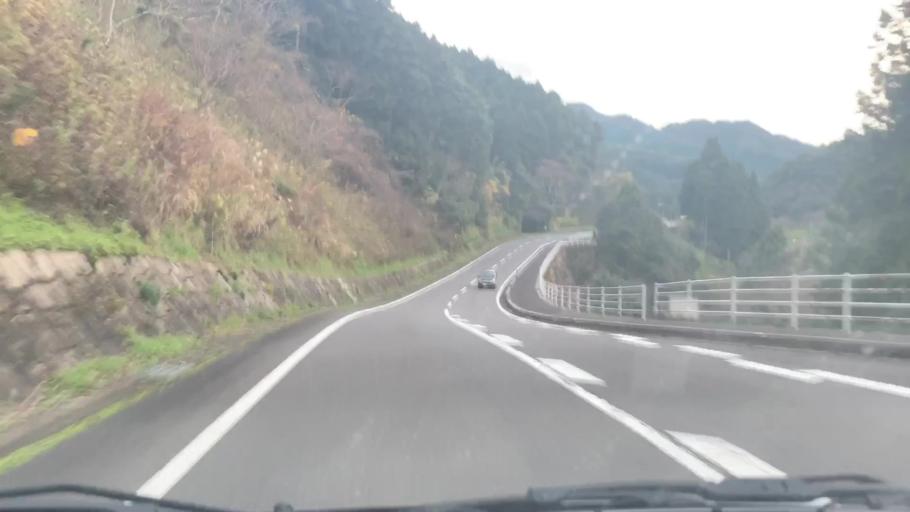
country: JP
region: Saga Prefecture
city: Kashima
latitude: 33.0233
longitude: 130.0669
